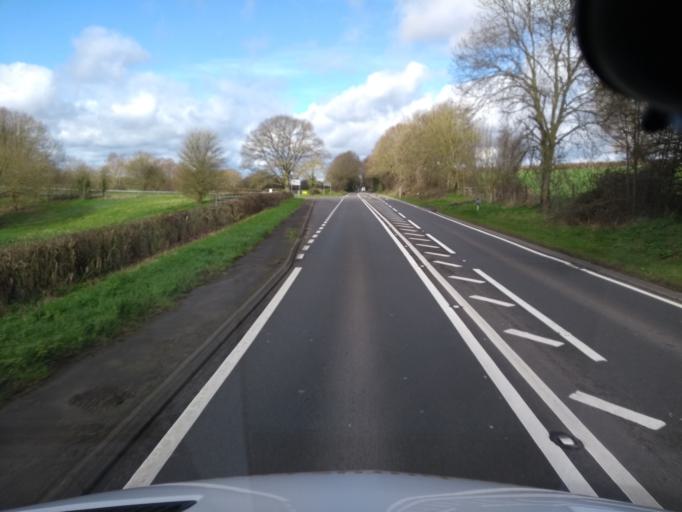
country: GB
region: England
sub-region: Somerset
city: Stoke-sub-Hamdon
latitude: 50.9582
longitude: -2.7197
